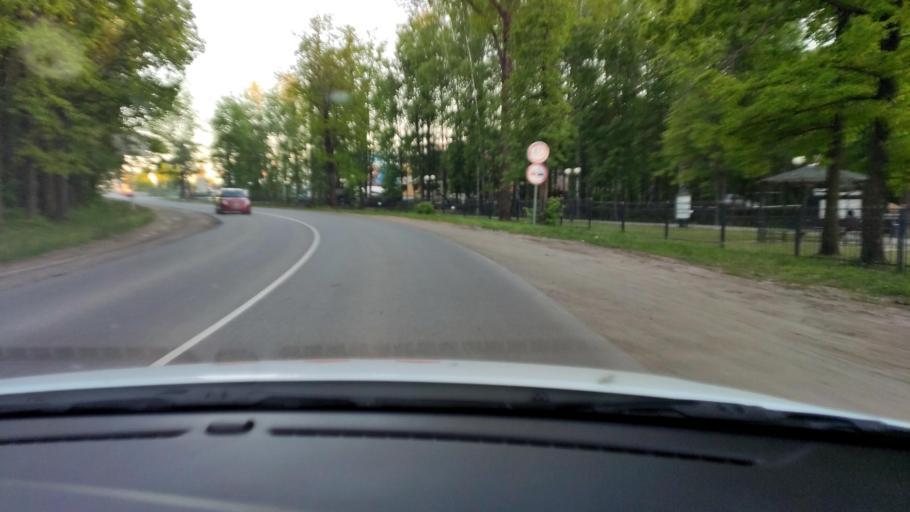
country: RU
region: Tatarstan
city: Vysokaya Gora
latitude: 55.9259
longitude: 49.3034
